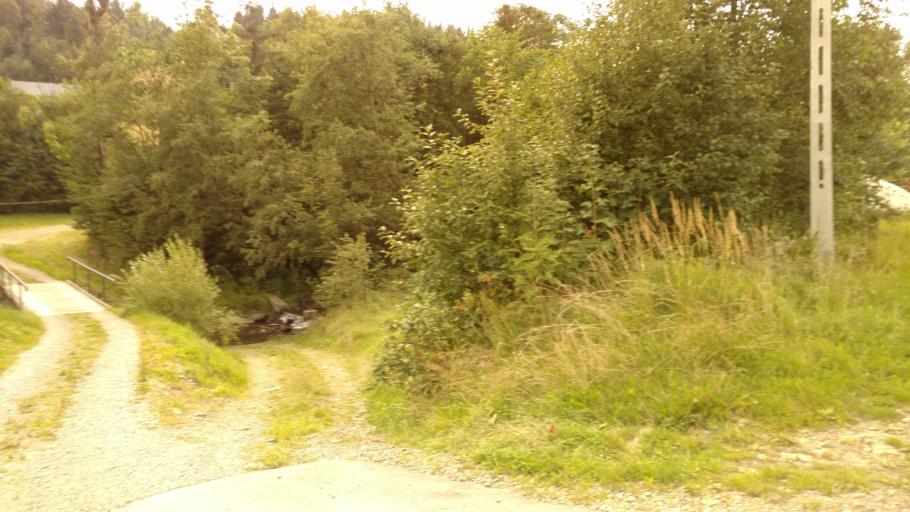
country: PL
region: Lesser Poland Voivodeship
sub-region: Powiat myslenicki
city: Skomielna Czarna
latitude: 49.7328
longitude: 19.8230
